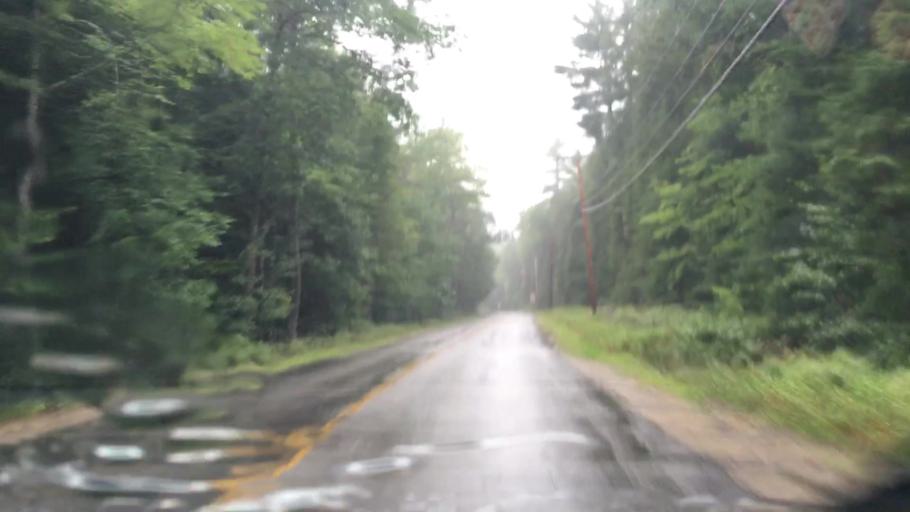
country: US
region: Maine
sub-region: Oxford County
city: Lovell
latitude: 44.0676
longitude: -70.8195
